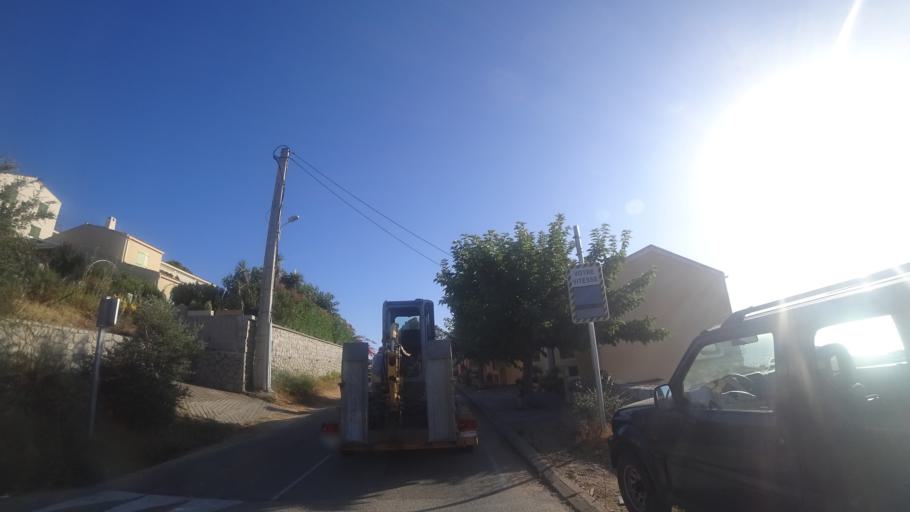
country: FR
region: Corsica
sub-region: Departement de la Corse-du-Sud
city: Cargese
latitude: 42.1377
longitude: 8.5972
